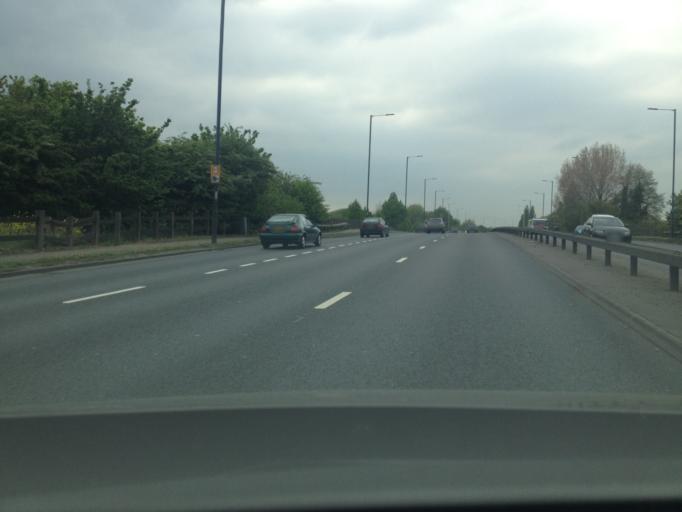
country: GB
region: England
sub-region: Greater London
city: Northolt
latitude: 51.5396
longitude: -0.3642
